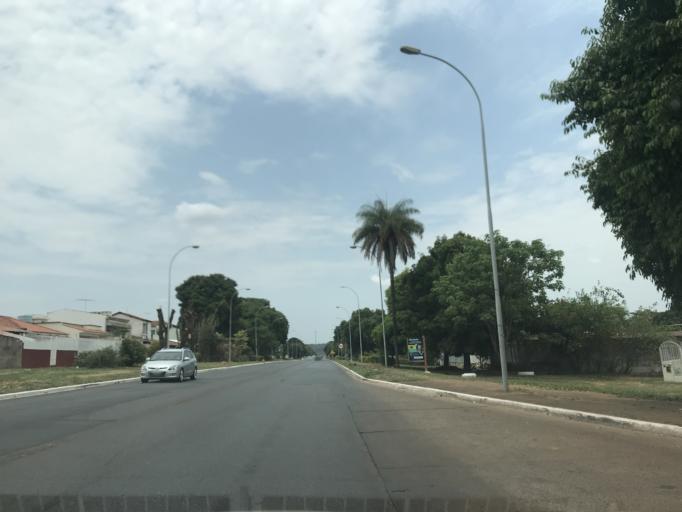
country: BR
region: Federal District
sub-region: Brasilia
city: Brasilia
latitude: -15.6537
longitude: -47.8045
